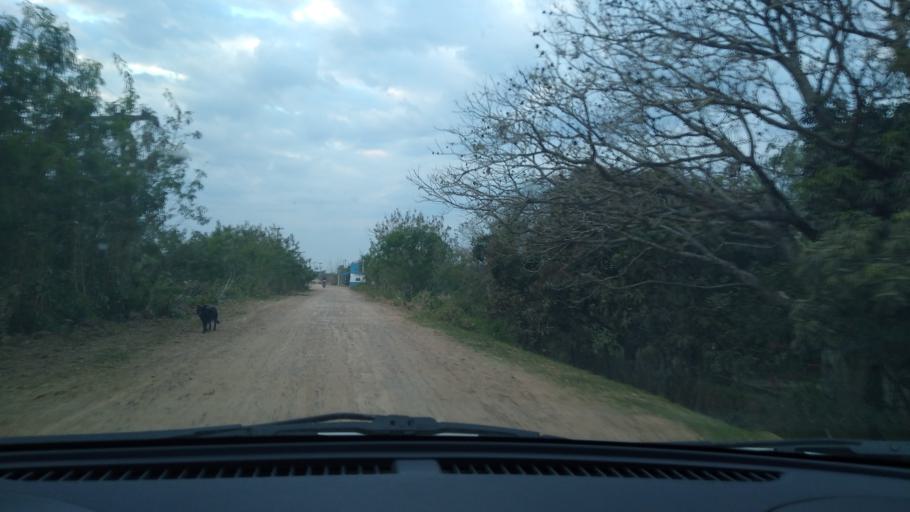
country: AR
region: Chaco
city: Barranqueras
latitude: -27.4678
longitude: -58.9391
